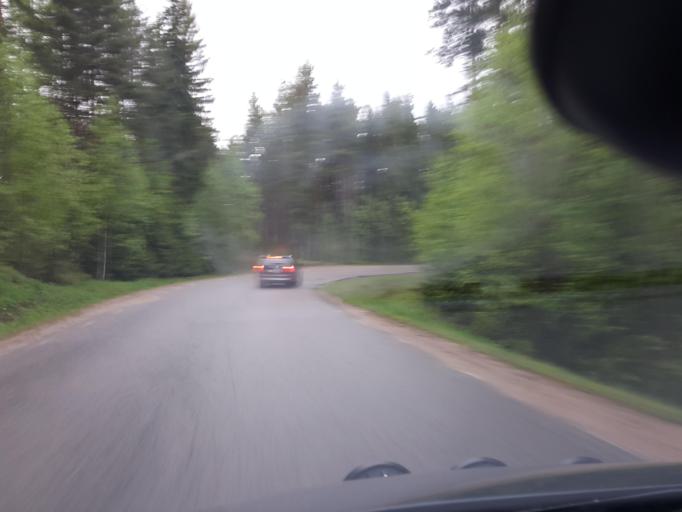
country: SE
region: Gaevleborg
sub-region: Ljusdals Kommun
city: Jaervsoe
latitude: 61.7827
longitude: 16.2157
